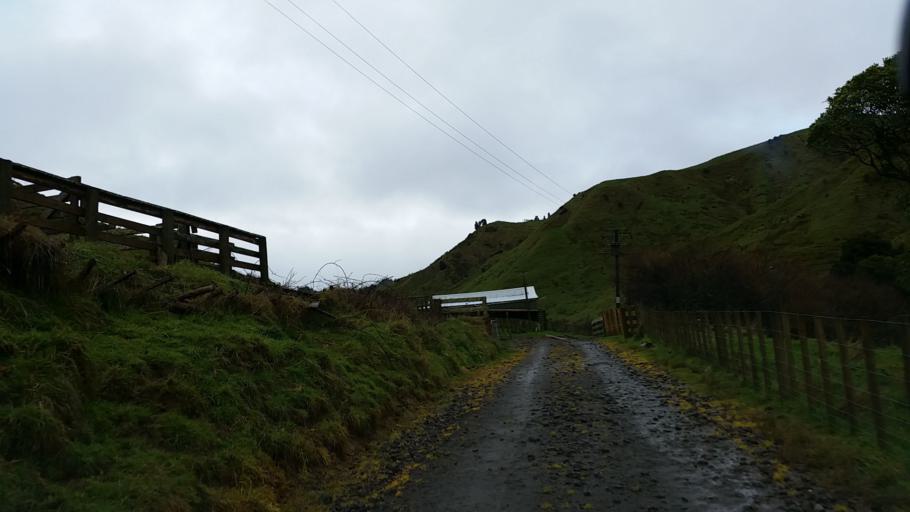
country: NZ
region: Taranaki
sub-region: South Taranaki District
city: Eltham
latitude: -39.4913
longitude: 174.4332
